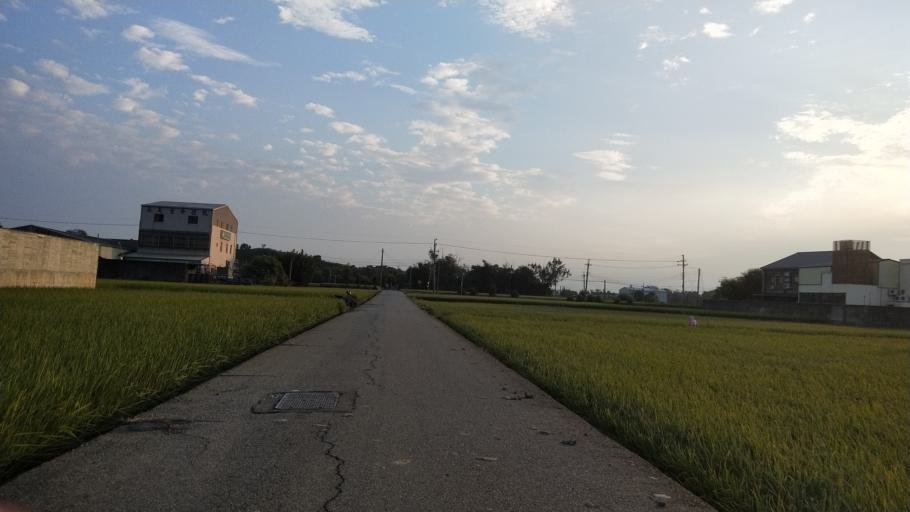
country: TW
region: Taiwan
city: Fengyuan
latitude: 24.4347
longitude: 120.6560
